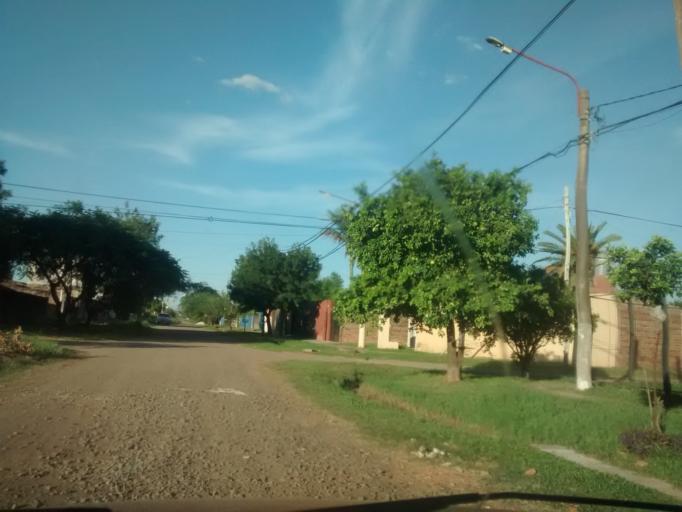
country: AR
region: Chaco
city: Fontana
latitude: -27.4537
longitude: -59.0230
